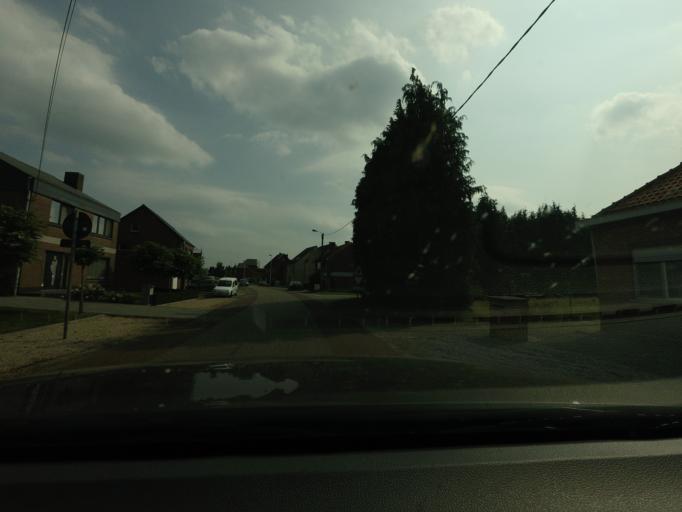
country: BE
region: Flanders
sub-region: Provincie Limburg
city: Leopoldsburg
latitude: 51.1112
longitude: 5.2335
